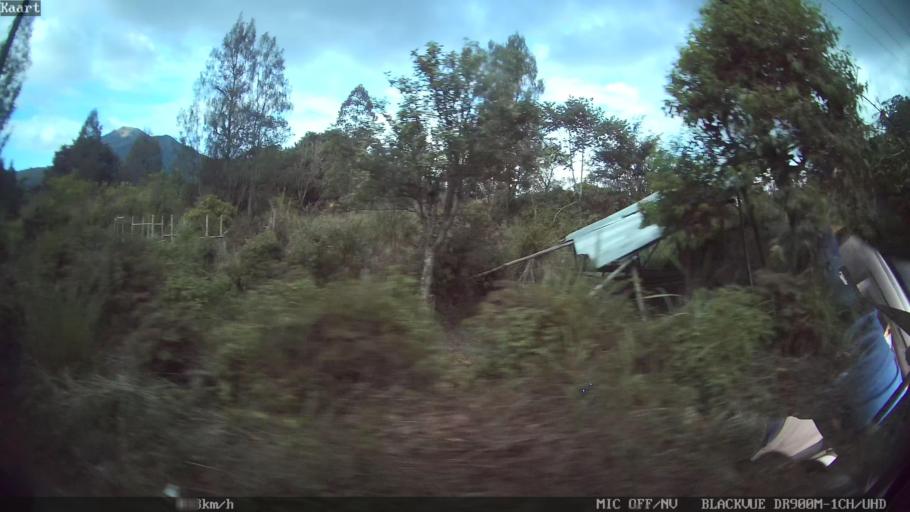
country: ID
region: Bali
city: Banjar Kedisan
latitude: -8.2482
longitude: 115.3476
